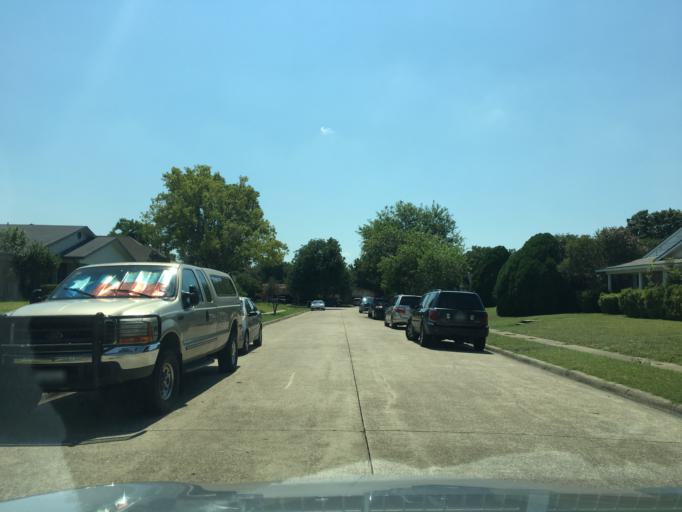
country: US
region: Texas
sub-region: Dallas County
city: Garland
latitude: 32.9540
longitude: -96.6669
